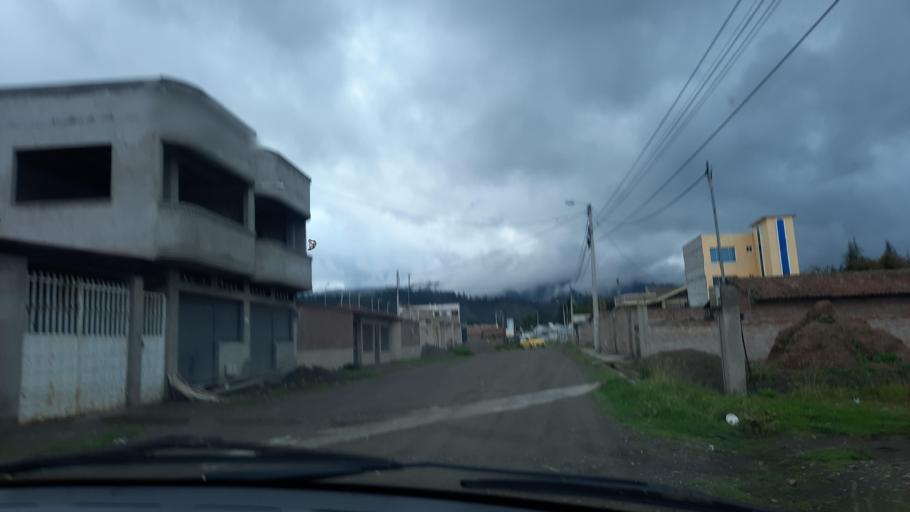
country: EC
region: Chimborazo
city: Riobamba
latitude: -1.6877
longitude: -78.6608
